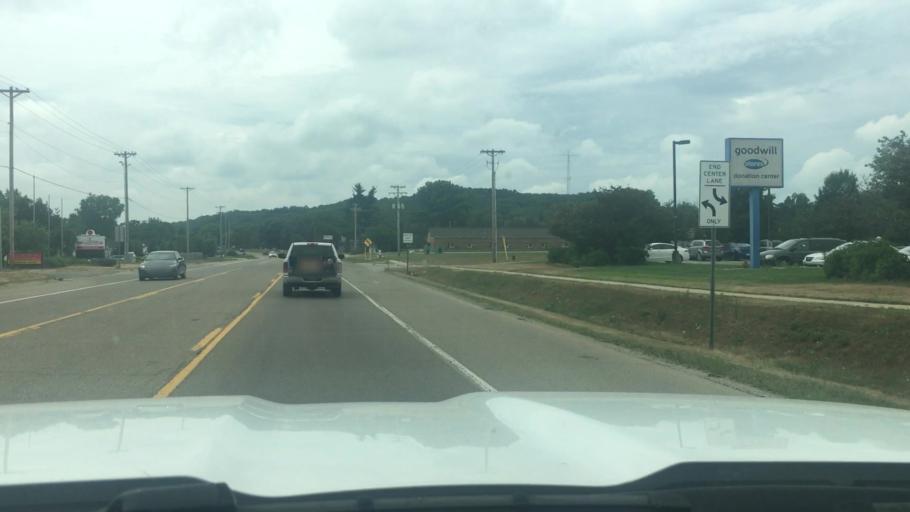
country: US
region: Michigan
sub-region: Kent County
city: Lowell
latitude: 42.9304
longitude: -85.3800
